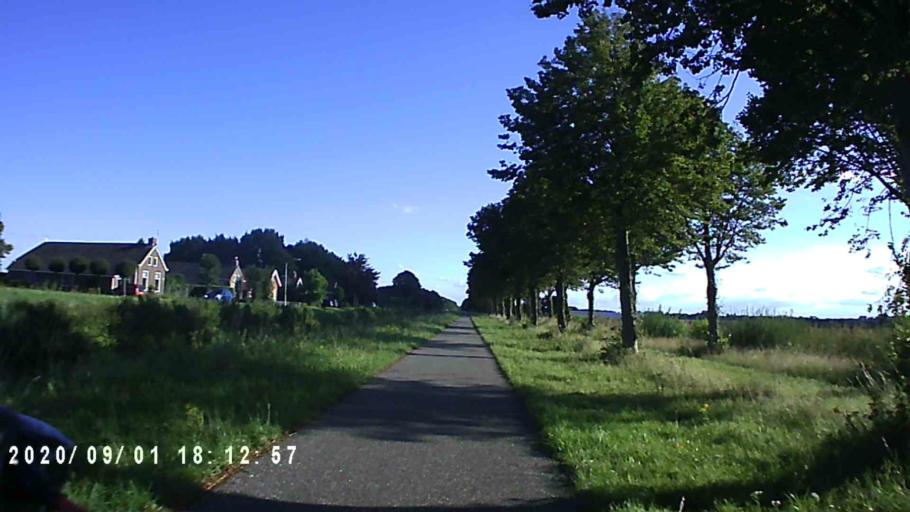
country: NL
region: Groningen
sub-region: Gemeente Hoogezand-Sappemeer
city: Sappemeer
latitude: 53.1852
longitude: 6.7857
